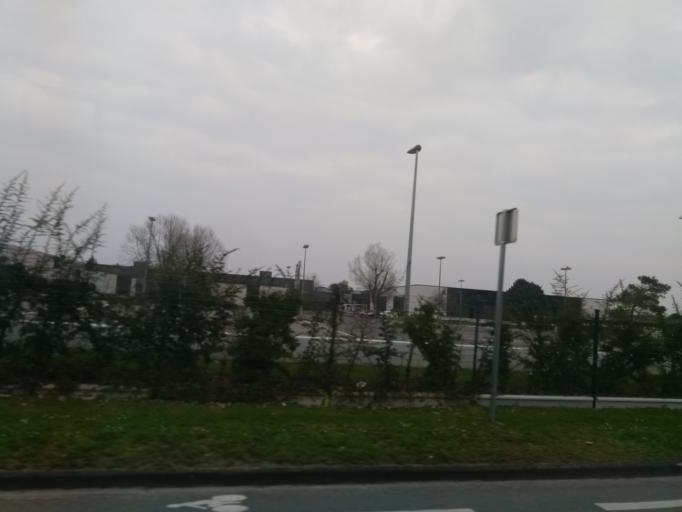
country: FR
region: Picardie
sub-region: Departement de l'Oise
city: Jaux
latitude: 49.3896
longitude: 2.7828
